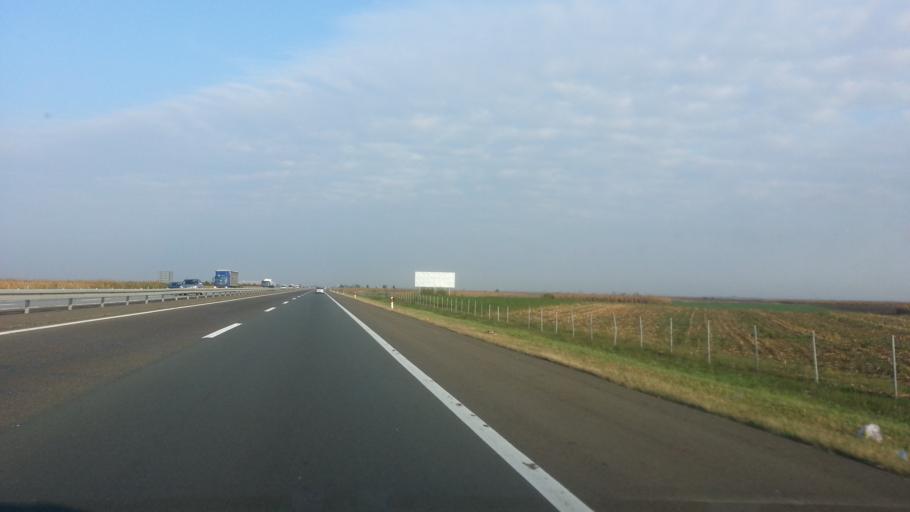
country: RS
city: Novi Banovci
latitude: 44.9530
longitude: 20.2647
